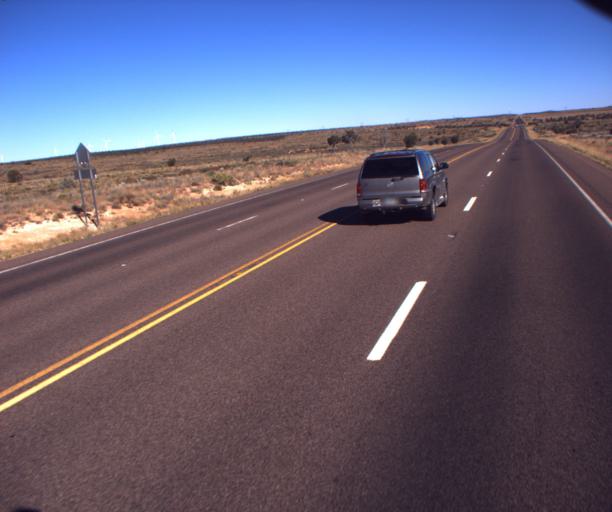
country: US
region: Arizona
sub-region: Navajo County
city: Snowflake
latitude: 34.5793
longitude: -110.0840
